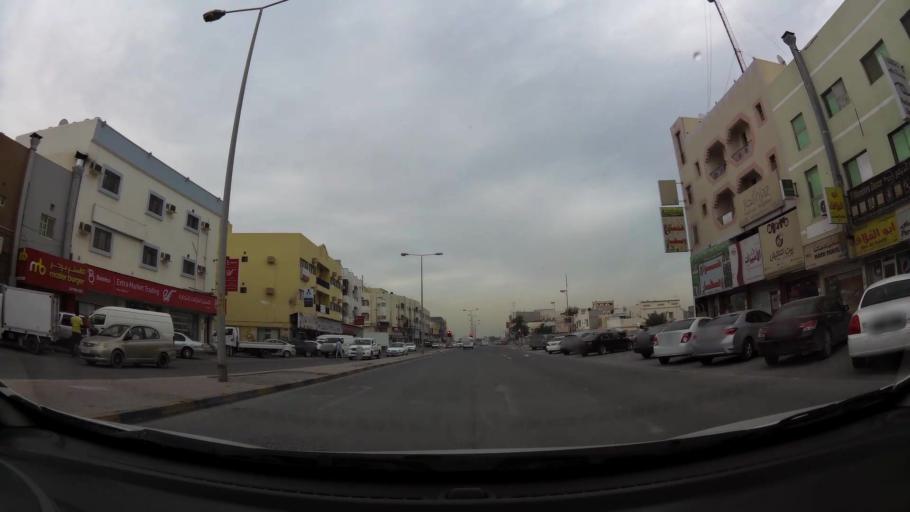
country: BH
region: Northern
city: Sitrah
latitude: 26.1652
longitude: 50.6091
